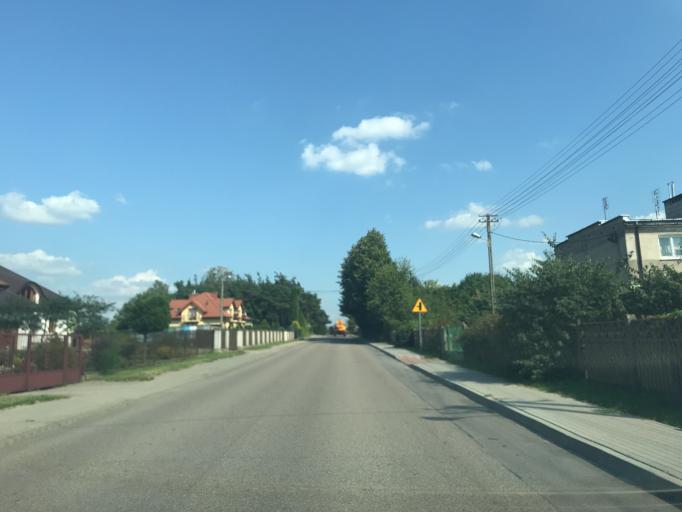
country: PL
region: Masovian Voivodeship
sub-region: Powiat mlawski
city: Mlawa
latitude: 53.1095
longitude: 20.3431
